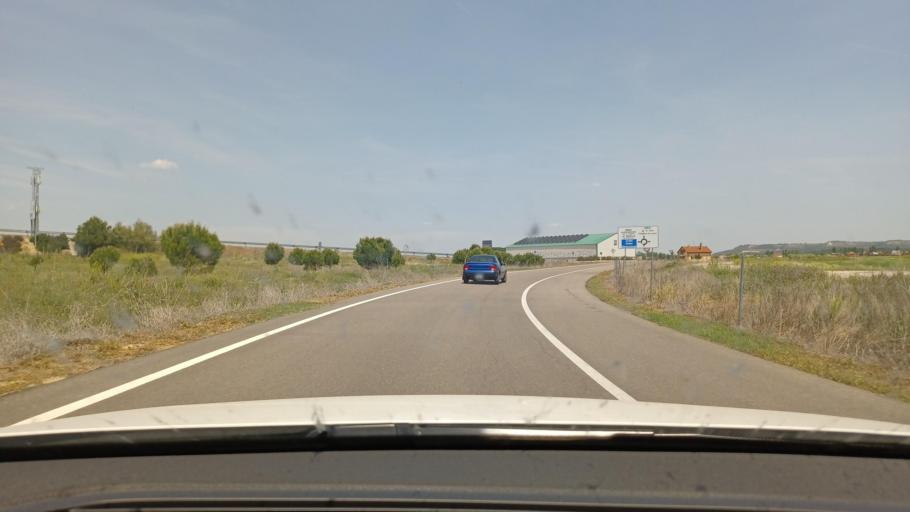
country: ES
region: Castille and Leon
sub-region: Provincia de Valladolid
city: Aldeamayor de San Martin
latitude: 41.5121
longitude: -4.6322
